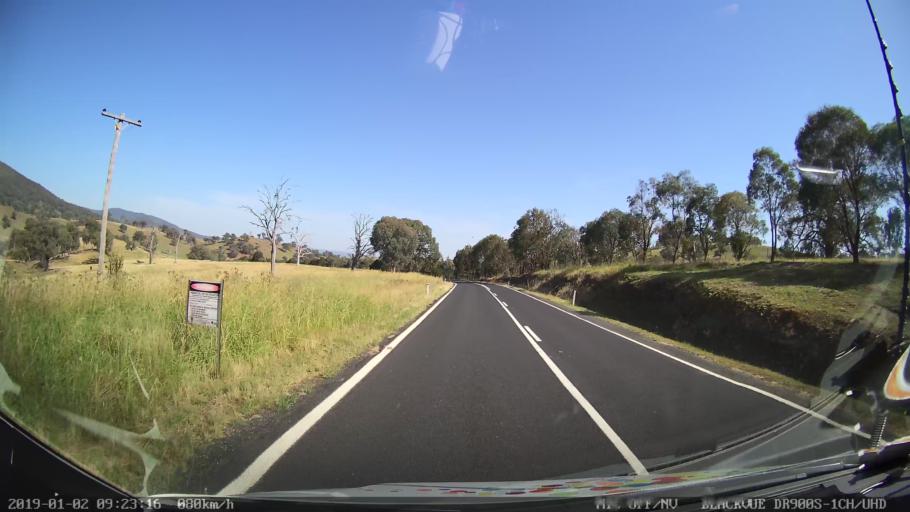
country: AU
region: New South Wales
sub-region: Tumut Shire
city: Tumut
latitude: -35.3892
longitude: 148.2978
